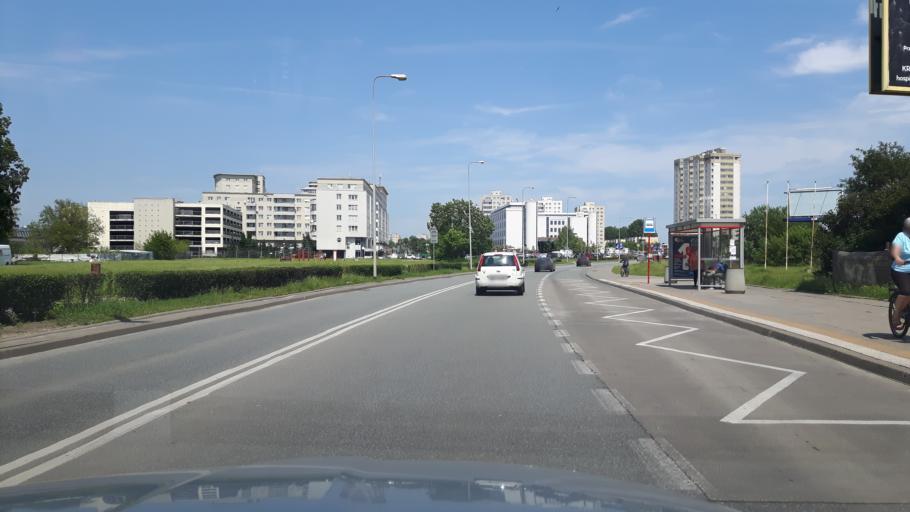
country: PL
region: Masovian Voivodeship
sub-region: Warszawa
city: Targowek
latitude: 52.2884
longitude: 21.0483
